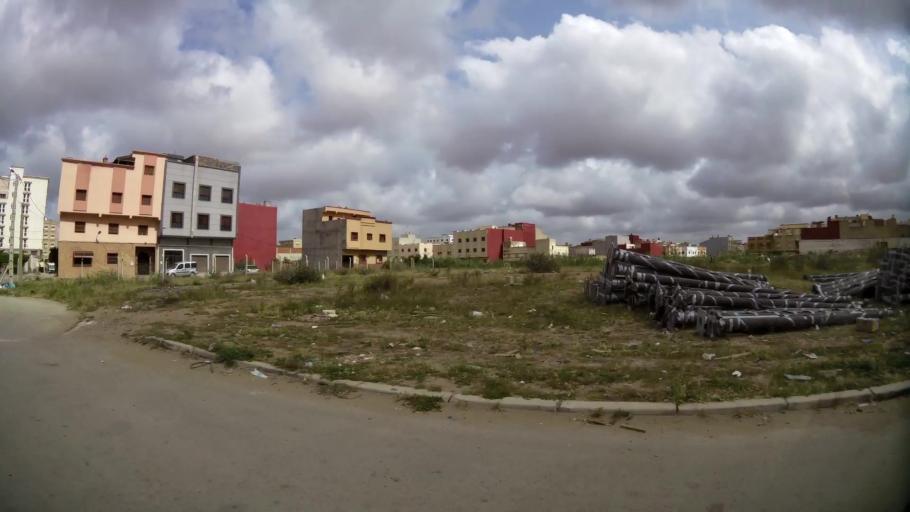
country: MA
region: Oriental
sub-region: Nador
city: Nador
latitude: 35.1587
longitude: -2.9322
